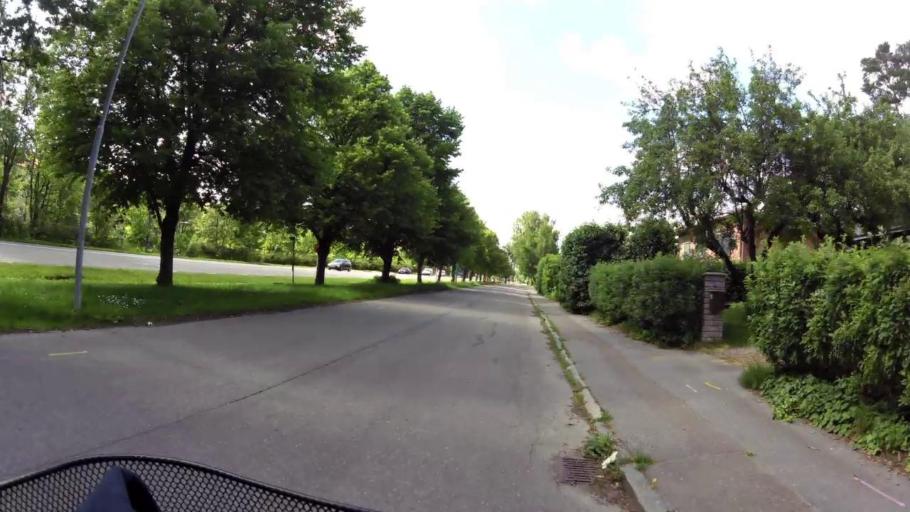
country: SE
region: OEstergoetland
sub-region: Linkopings Kommun
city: Linkoping
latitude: 58.3919
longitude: 15.6475
